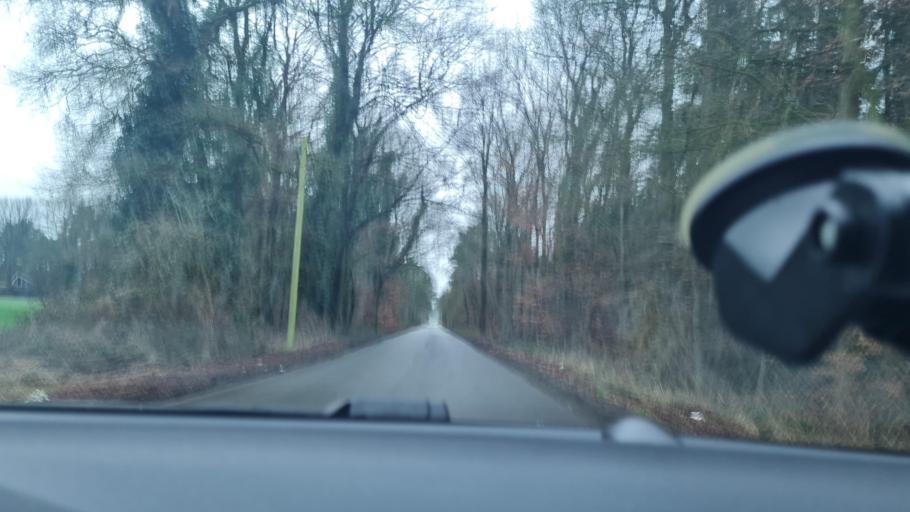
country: DE
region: North Rhine-Westphalia
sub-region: Regierungsbezirk Munster
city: Raesfeld
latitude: 51.7603
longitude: 6.8989
